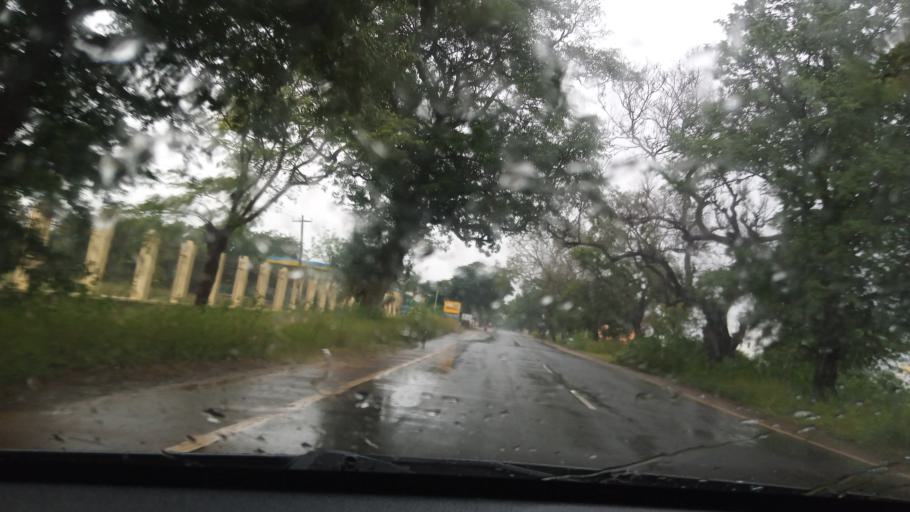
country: IN
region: Tamil Nadu
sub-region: Vellore
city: Kalavai
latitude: 12.8011
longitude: 79.4358
